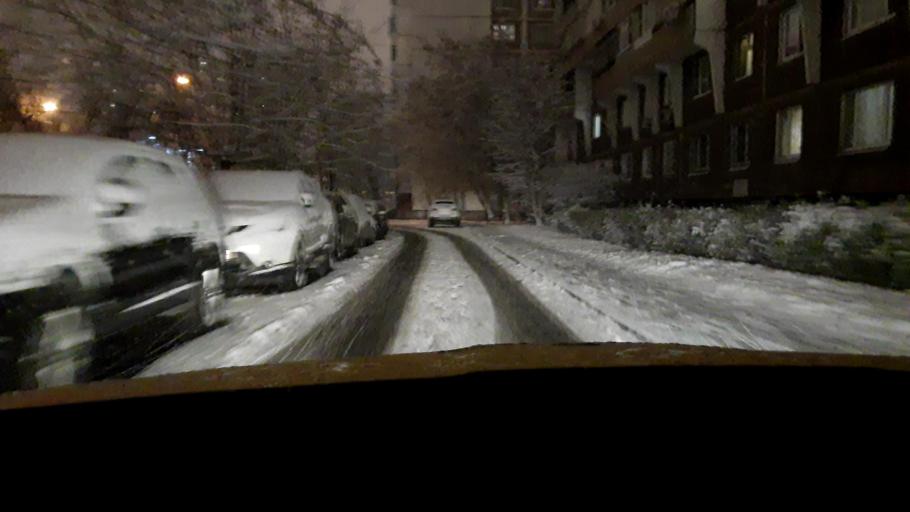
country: RU
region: Moscow
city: Mar'ino
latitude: 55.6491
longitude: 37.7347
